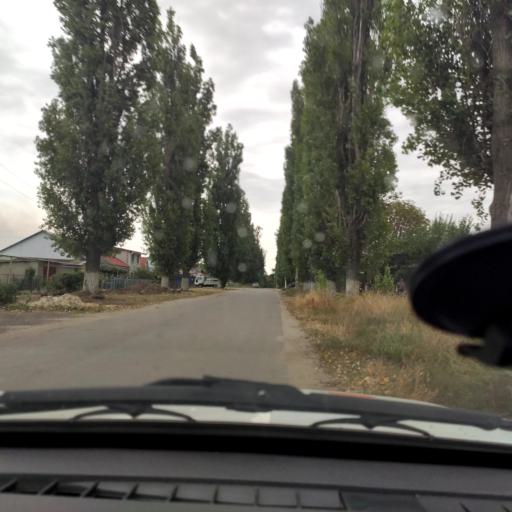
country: RU
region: Voronezj
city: Strelitsa
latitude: 51.6075
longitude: 38.9062
